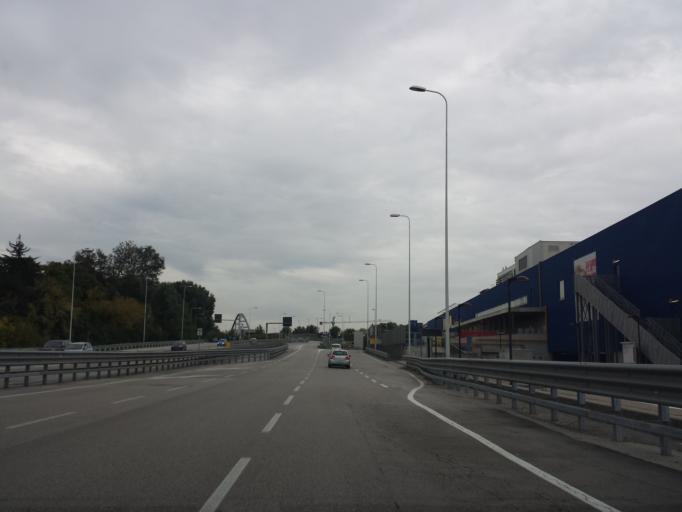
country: IT
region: Veneto
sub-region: Provincia di Padova
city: Noventa
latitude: 45.4193
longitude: 11.9311
